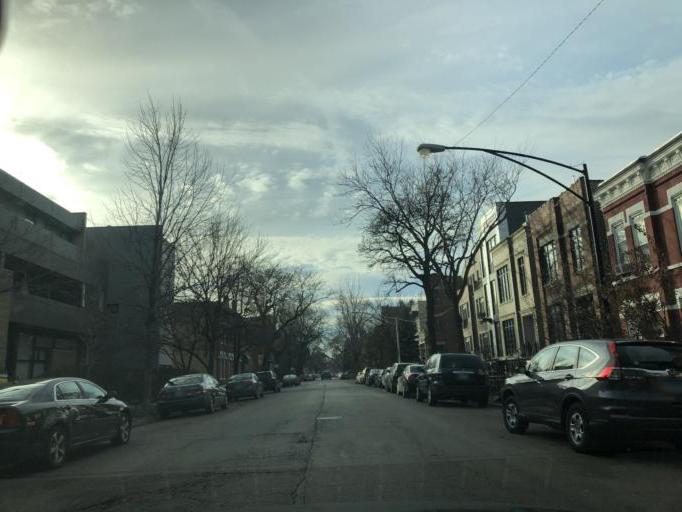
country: US
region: Illinois
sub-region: Cook County
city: Chicago
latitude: 41.8987
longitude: -87.6747
